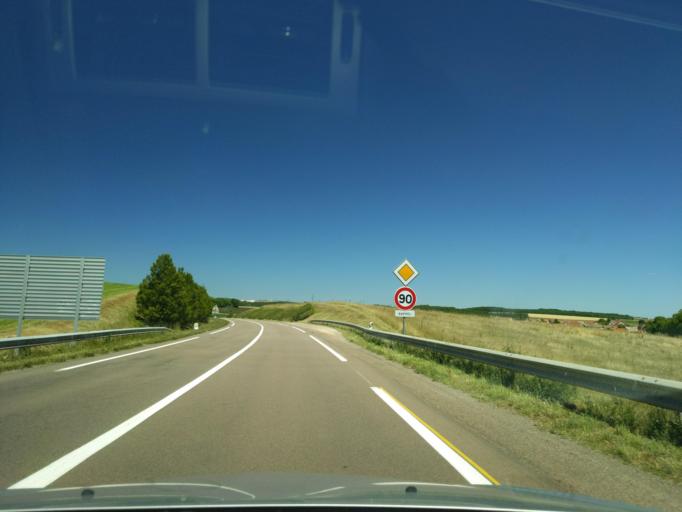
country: FR
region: Bourgogne
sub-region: Departement de la Cote-d'Or
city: Ruffey-les-Echirey
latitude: 47.4039
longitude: 5.0722
